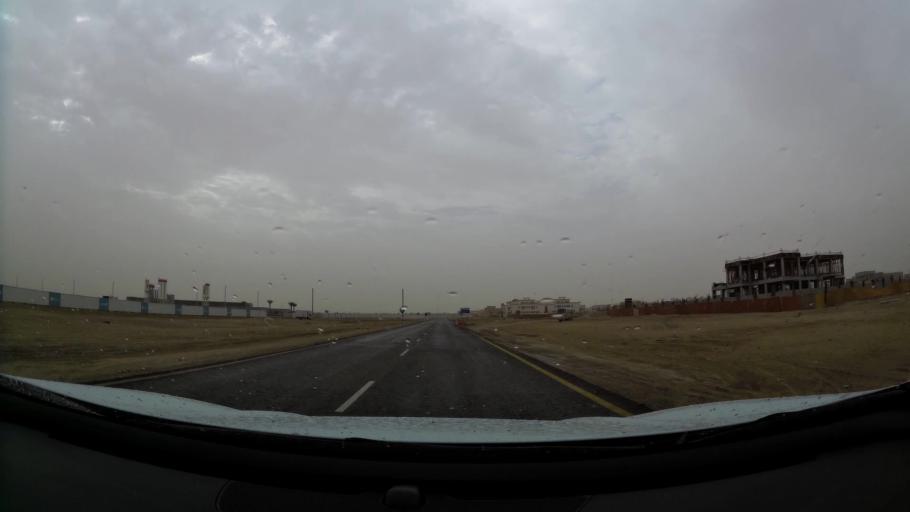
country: AE
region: Abu Dhabi
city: Abu Dhabi
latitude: 24.4187
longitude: 54.6088
